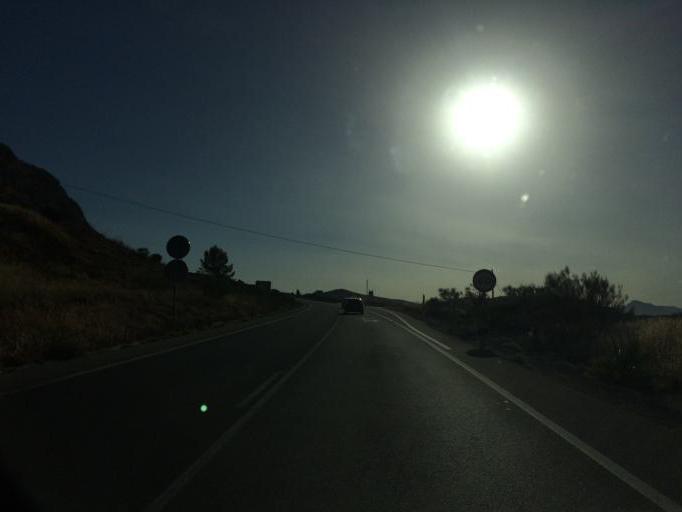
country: ES
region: Andalusia
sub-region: Provincia de Malaga
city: Teba
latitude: 36.9640
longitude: -4.8520
